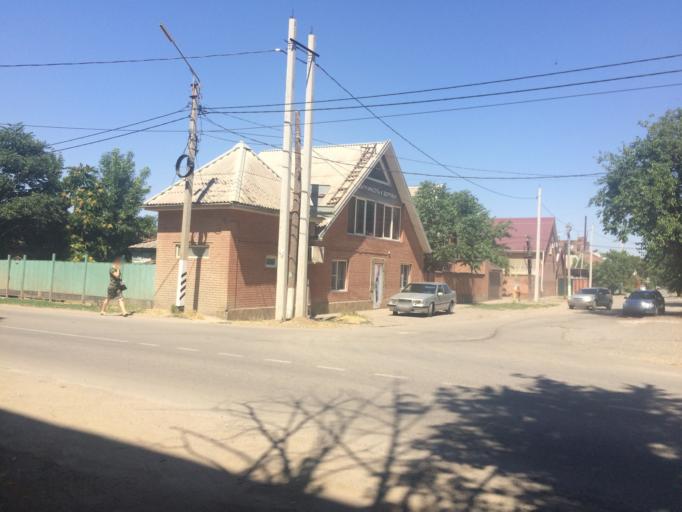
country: RU
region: Rostov
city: Sal'sk
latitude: 46.4697
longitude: 41.5415
